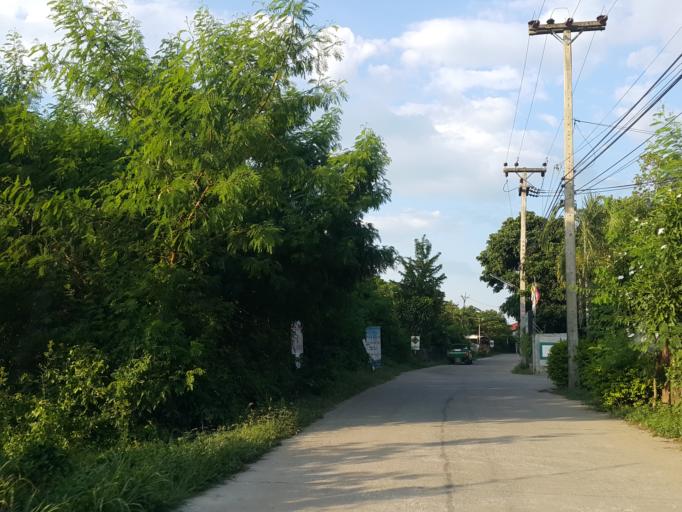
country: TH
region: Chiang Mai
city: San Kamphaeng
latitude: 18.7483
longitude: 99.1056
